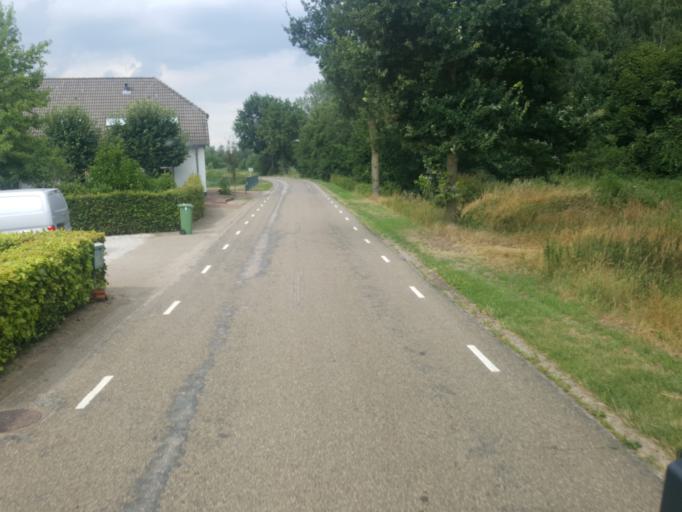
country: NL
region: North Brabant
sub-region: Gemeente Mill en Sint Hubert
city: Wilbertoord
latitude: 51.6899
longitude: 5.8152
